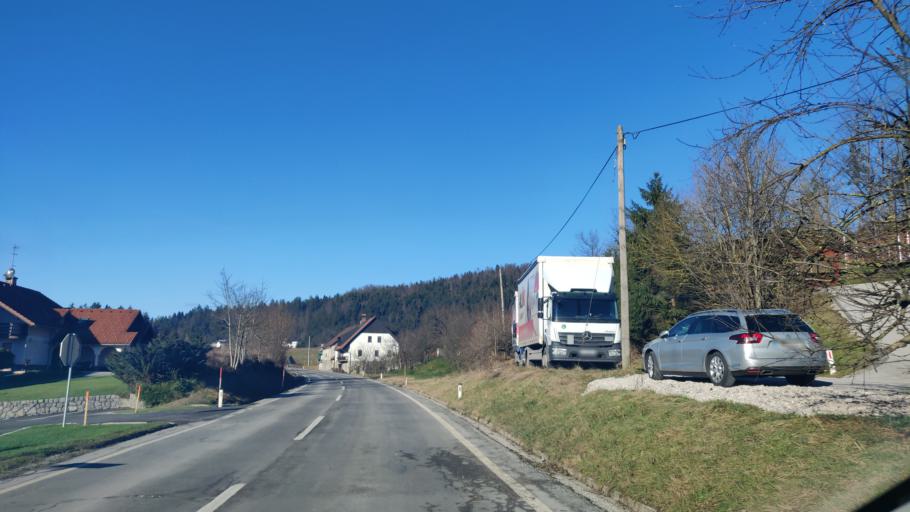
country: SI
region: Logatec
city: Logatec
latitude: 45.8733
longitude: 14.2131
